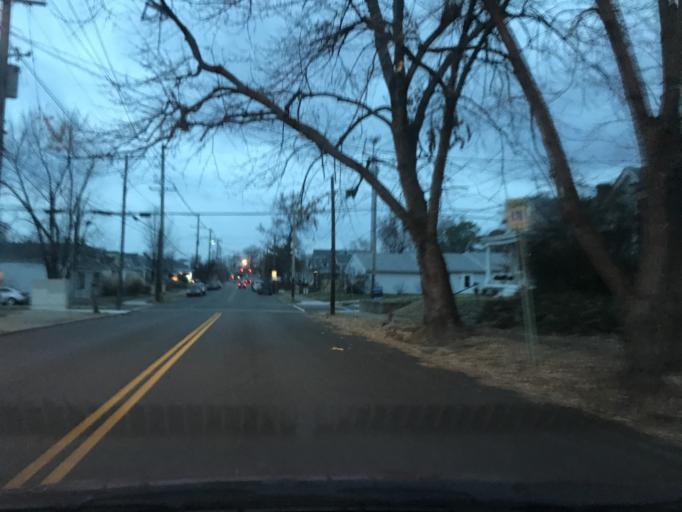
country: US
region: Kentucky
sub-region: Jefferson County
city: Audubon Park
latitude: 38.2235
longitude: -85.7402
